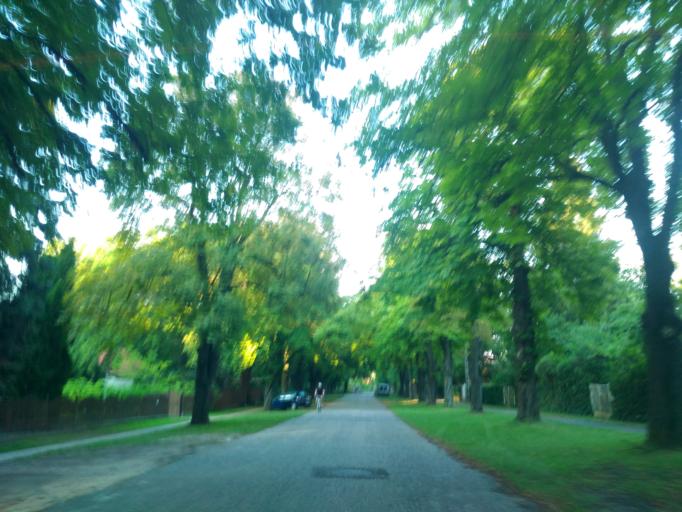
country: HU
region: Somogy
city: Balatonszarszo
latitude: 46.8133
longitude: 17.7830
